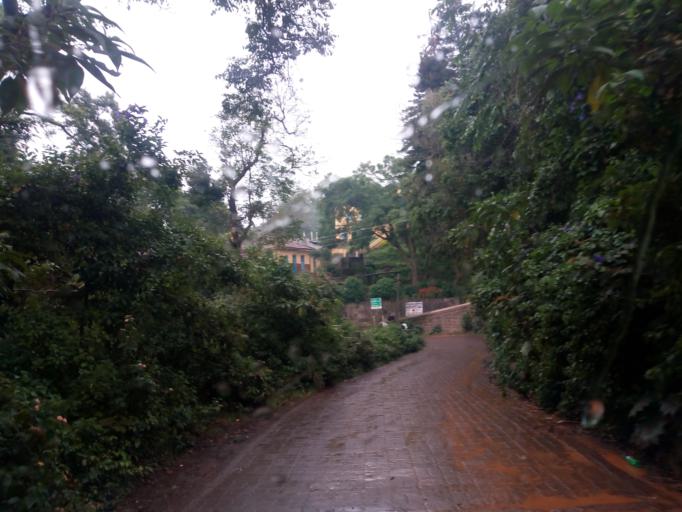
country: IN
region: Tamil Nadu
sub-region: Nilgiri
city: Wellington
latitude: 11.3501
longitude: 76.8114
